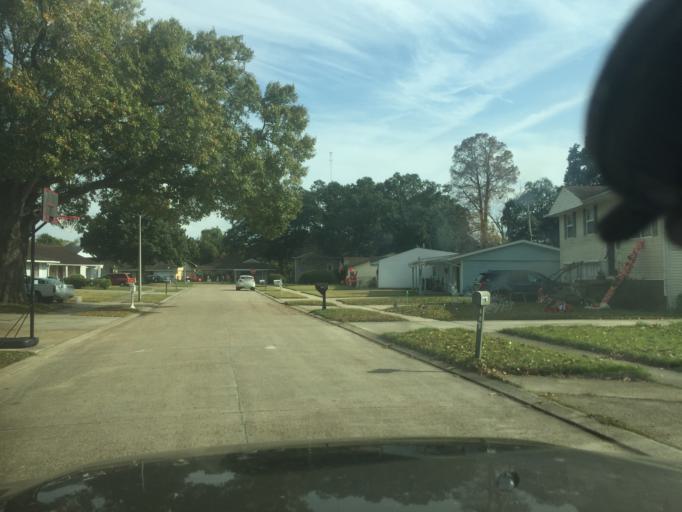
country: US
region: Louisiana
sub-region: Jefferson Parish
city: Avondale
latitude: 29.9125
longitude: -90.2030
